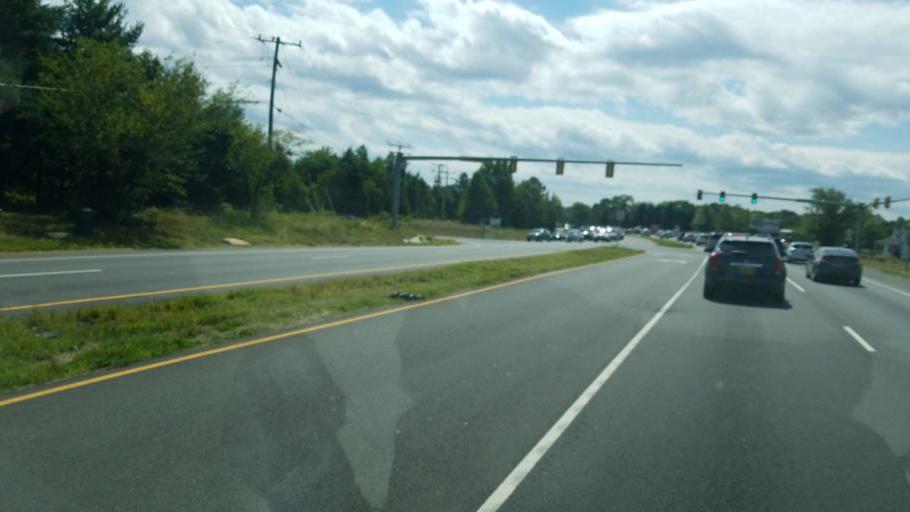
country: US
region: Virginia
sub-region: Stafford County
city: Falmouth
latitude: 38.3823
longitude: -77.5435
